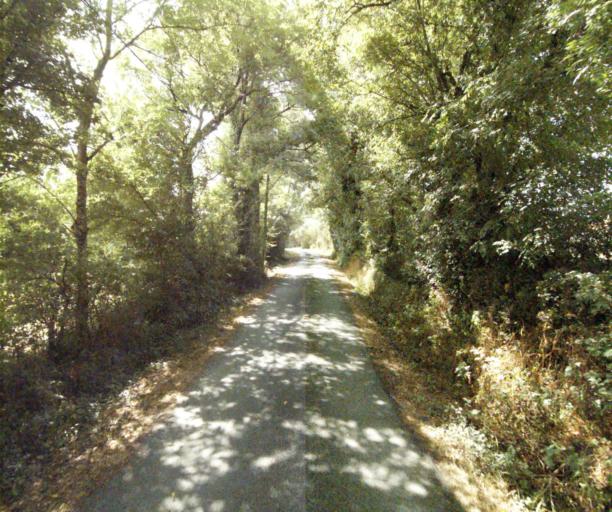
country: FR
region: Midi-Pyrenees
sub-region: Departement du Tarn
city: Dourgne
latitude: 43.4875
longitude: 2.1084
